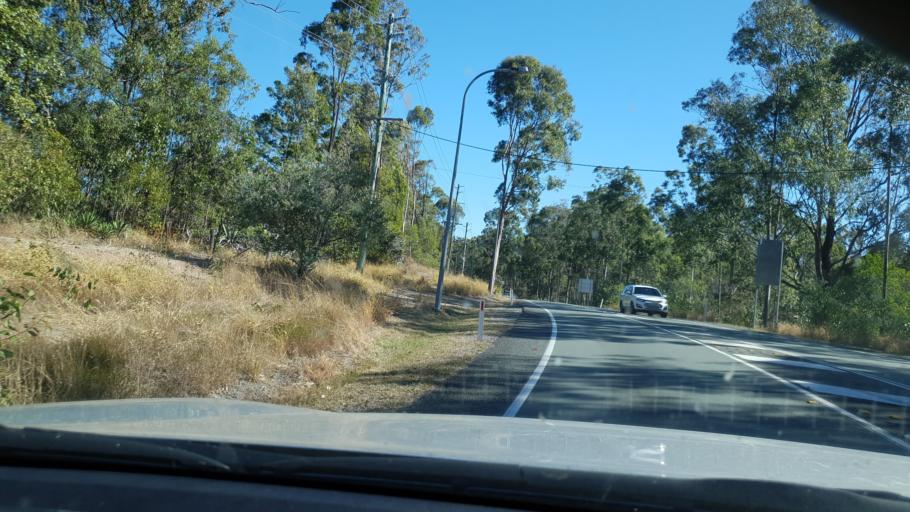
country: AU
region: Queensland
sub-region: Moreton Bay
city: Strathpine
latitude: -27.3279
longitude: 152.9341
